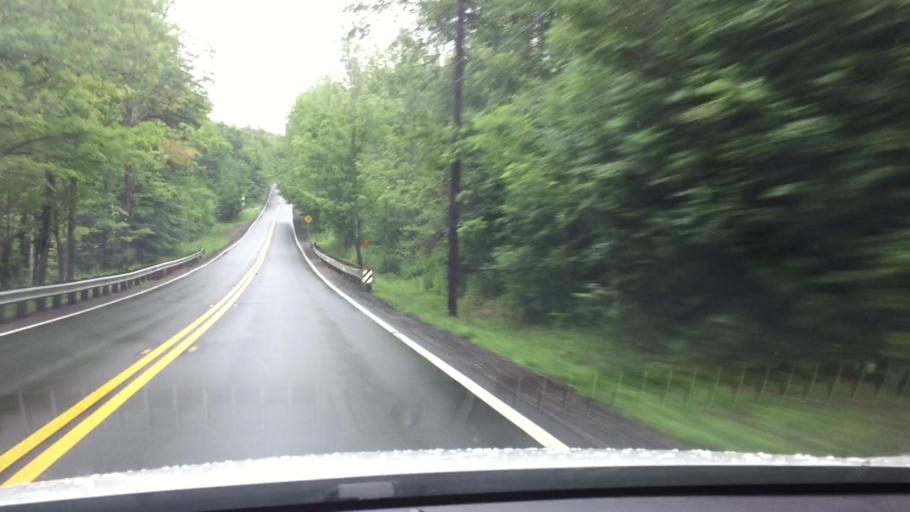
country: US
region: Massachusetts
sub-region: Berkshire County
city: Becket
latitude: 42.3582
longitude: -73.1337
